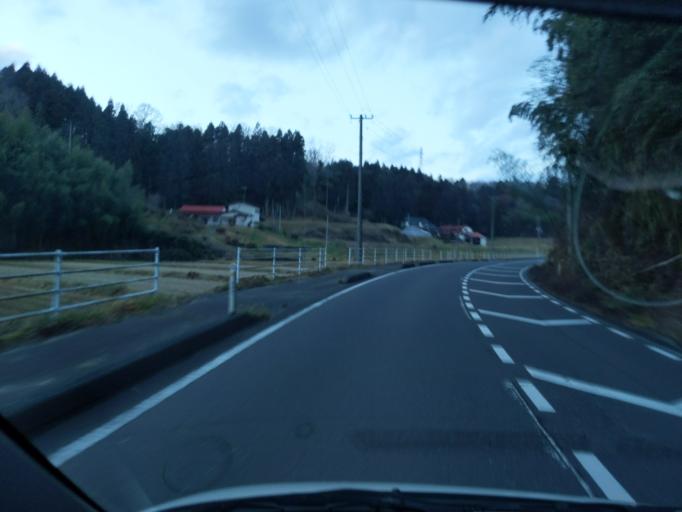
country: JP
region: Iwate
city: Ichinoseki
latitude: 38.8118
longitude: 141.1162
